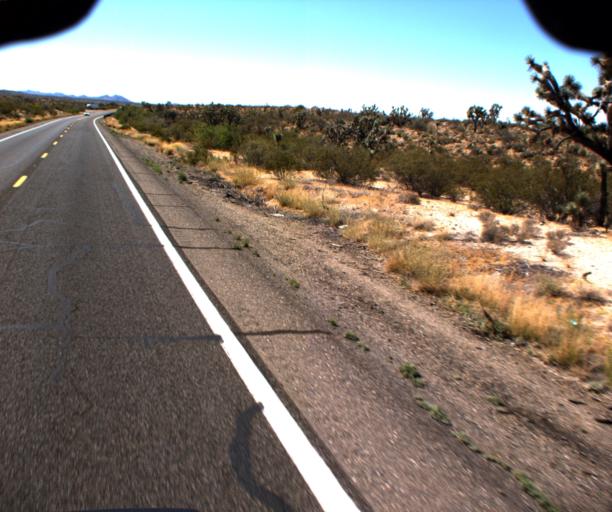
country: US
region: Arizona
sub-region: Yavapai County
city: Congress
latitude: 34.2347
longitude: -113.0726
